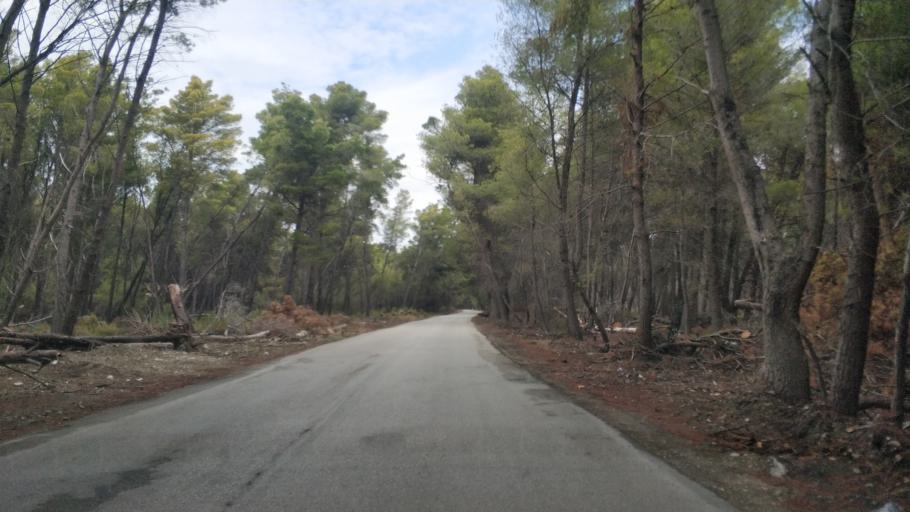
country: AL
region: Vlore
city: Vlore
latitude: 40.4830
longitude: 19.4476
